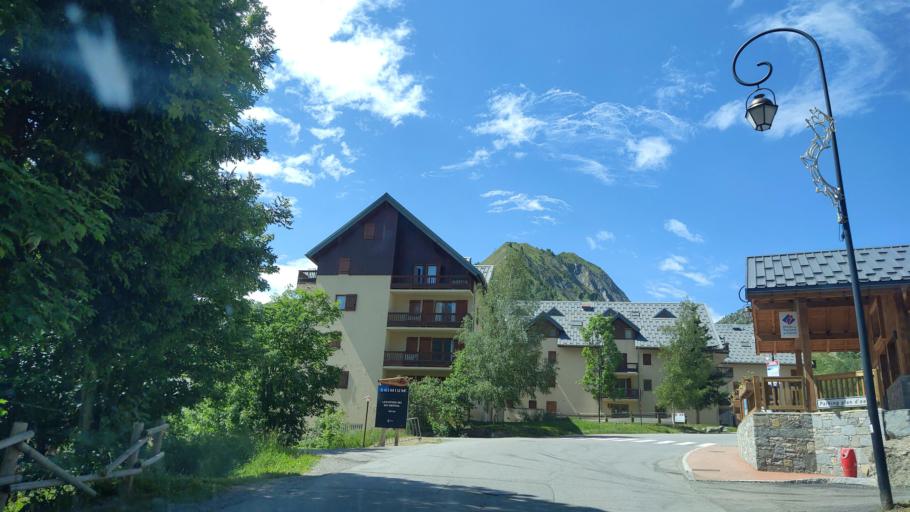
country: FR
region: Rhone-Alpes
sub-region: Departement de la Savoie
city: Saint-Etienne-de-Cuines
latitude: 45.2212
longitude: 6.2202
